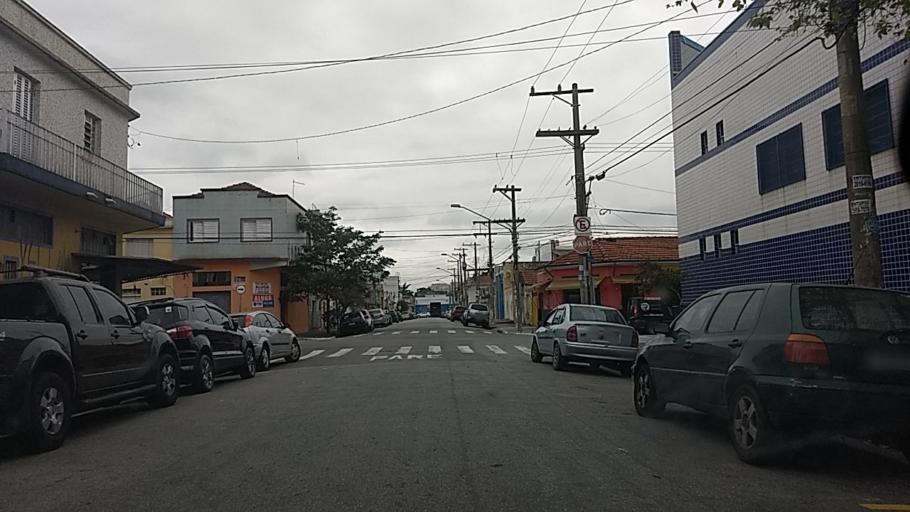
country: BR
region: Sao Paulo
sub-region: Sao Paulo
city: Sao Paulo
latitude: -23.5179
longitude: -46.5936
